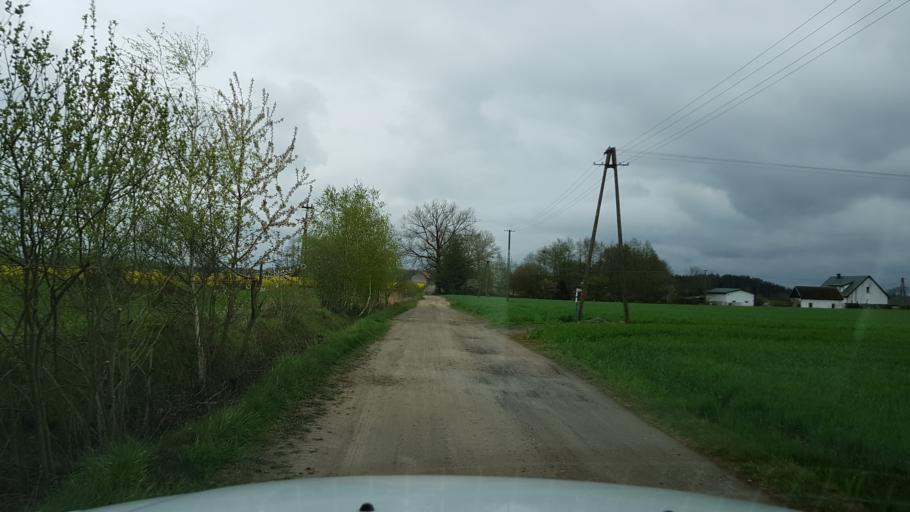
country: PL
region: West Pomeranian Voivodeship
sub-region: Powiat kolobrzeski
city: Ryman
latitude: 54.0343
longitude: 15.4739
